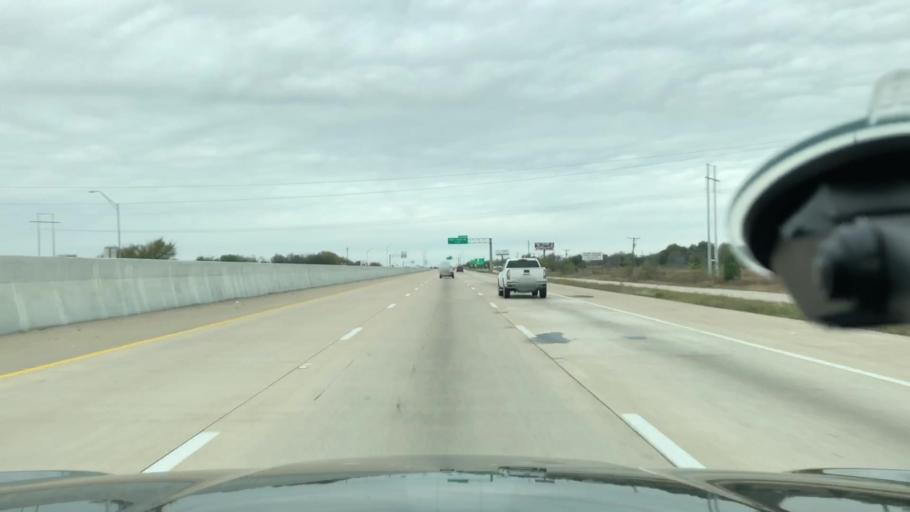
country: US
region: Texas
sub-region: Ellis County
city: Red Oak
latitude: 32.5419
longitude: -96.8222
